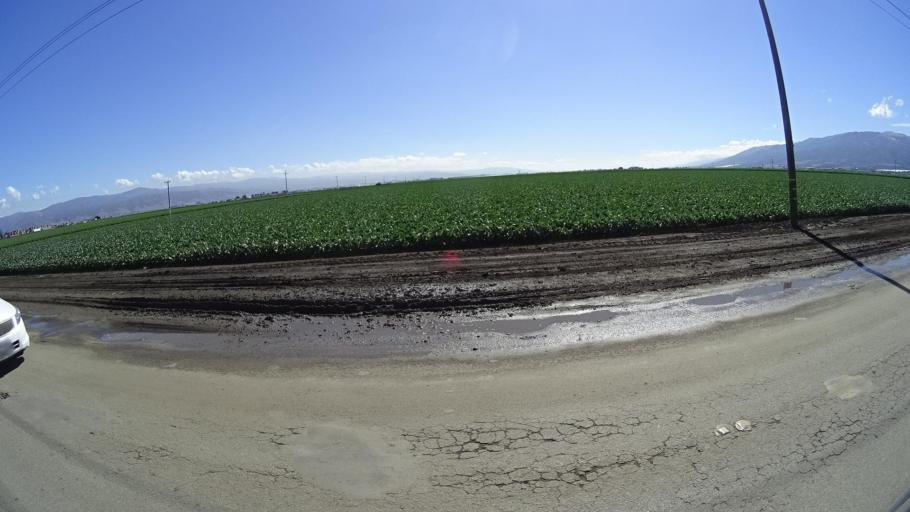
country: US
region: California
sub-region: Monterey County
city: Salinas
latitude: 36.6419
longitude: -121.6368
